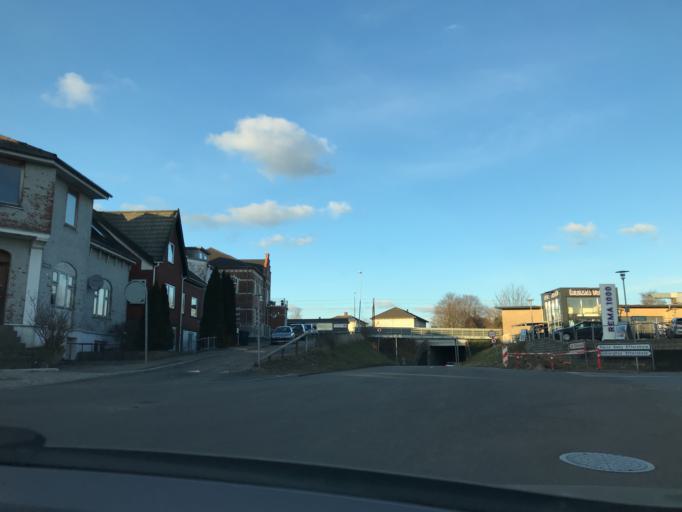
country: DK
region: South Denmark
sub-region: Middelfart Kommune
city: Norre Aby
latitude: 55.4587
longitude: 9.8712
